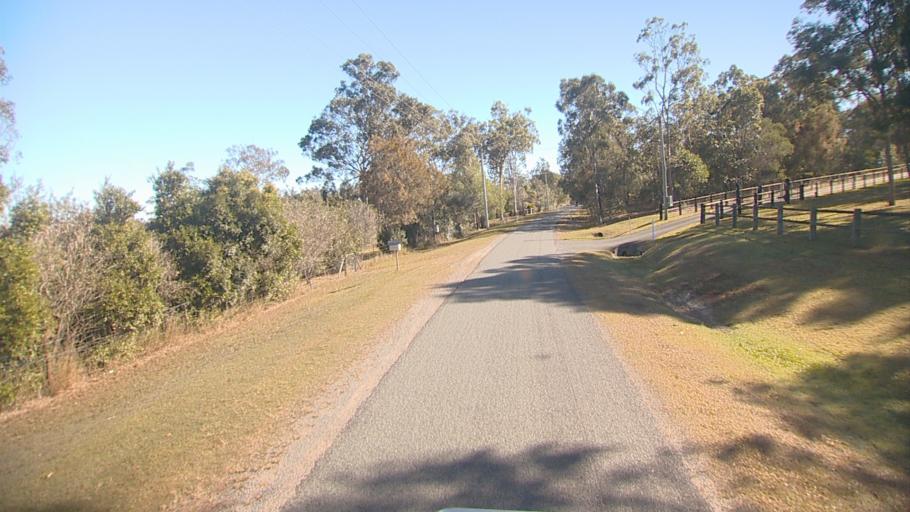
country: AU
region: Queensland
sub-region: Logan
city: Chambers Flat
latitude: -27.7731
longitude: 153.1253
